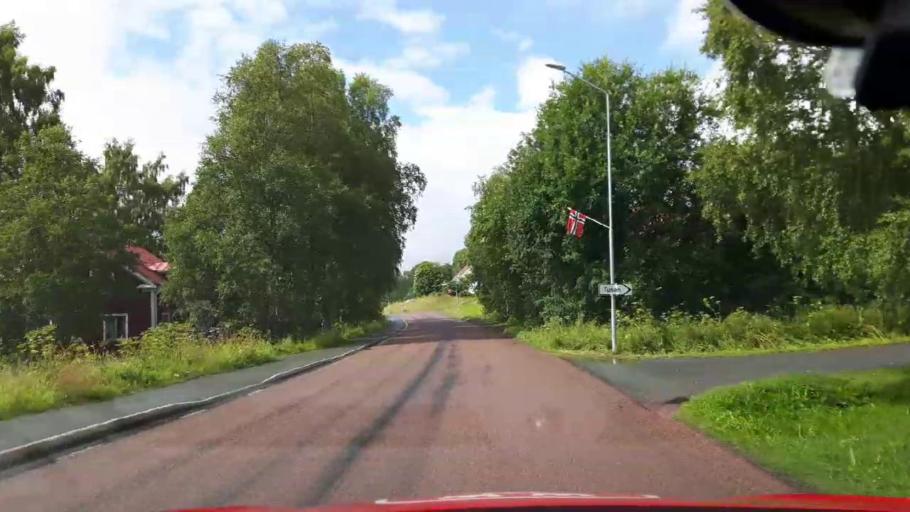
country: SE
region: Jaemtland
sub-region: Krokoms Kommun
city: Valla
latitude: 63.3852
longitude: 13.9338
